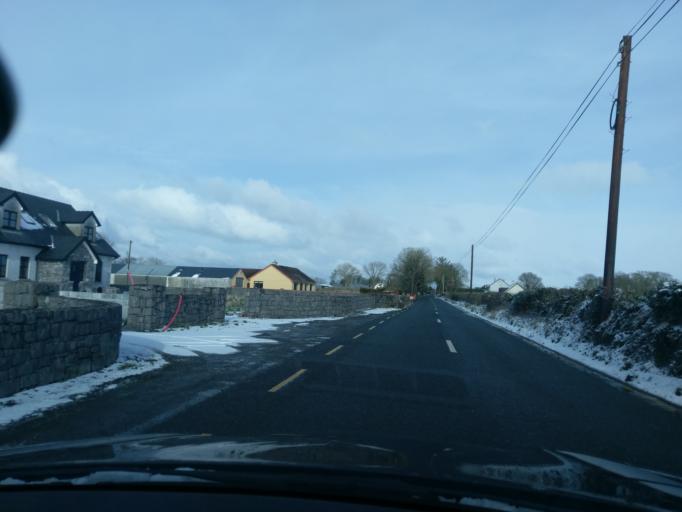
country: IE
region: Connaught
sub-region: County Galway
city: Athenry
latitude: 53.1842
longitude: -8.7732
